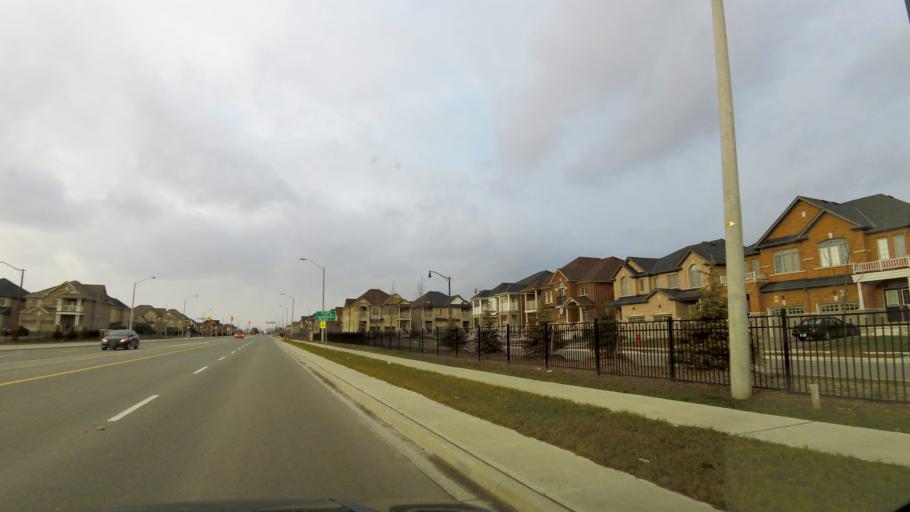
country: CA
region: Ontario
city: Brampton
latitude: 43.7967
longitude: -79.6727
